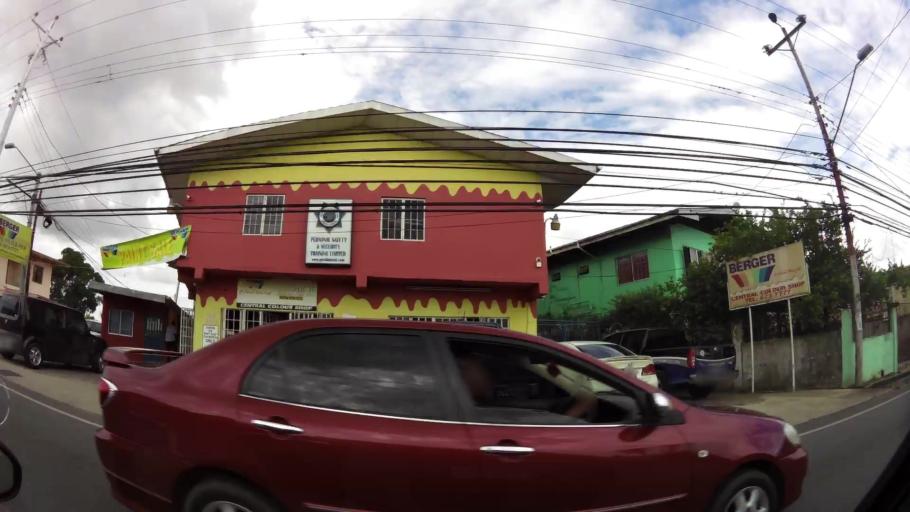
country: TT
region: Chaguanas
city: Chaguanas
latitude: 10.4712
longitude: -61.4142
